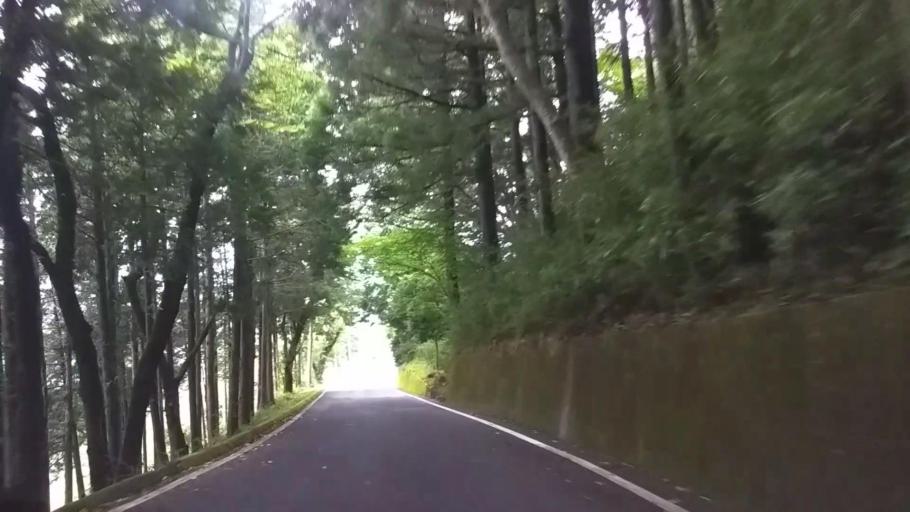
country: JP
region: Shizuoka
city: Gotemba
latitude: 35.3292
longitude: 138.9838
